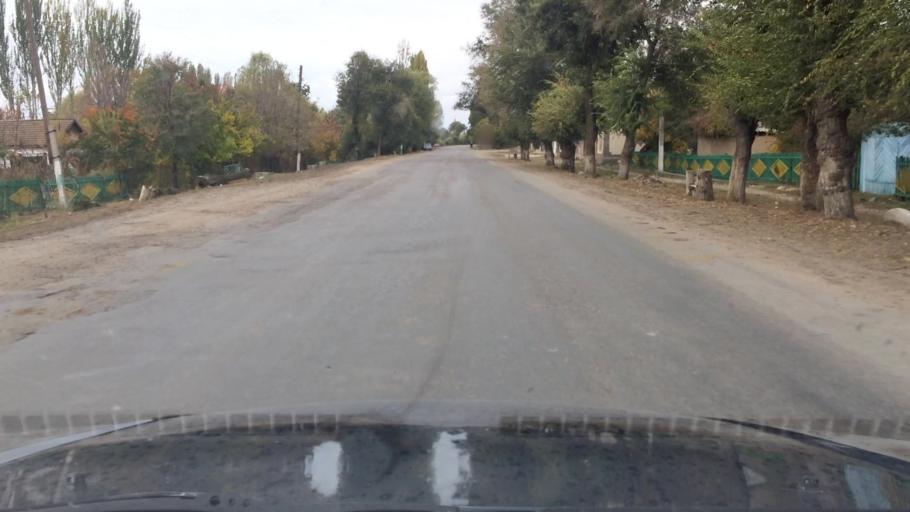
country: KG
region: Ysyk-Koel
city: Pokrovka
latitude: 42.7371
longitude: 77.9373
